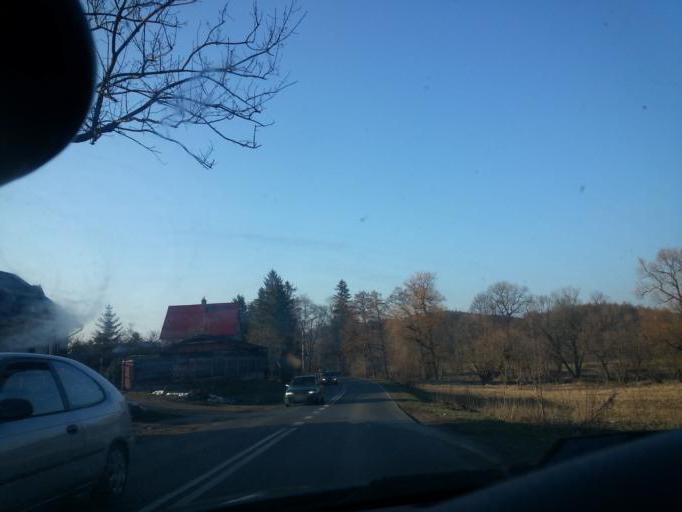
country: PL
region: Lower Silesian Voivodeship
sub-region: Powiat jeleniogorski
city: Myslakowice
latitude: 50.8215
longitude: 15.8045
